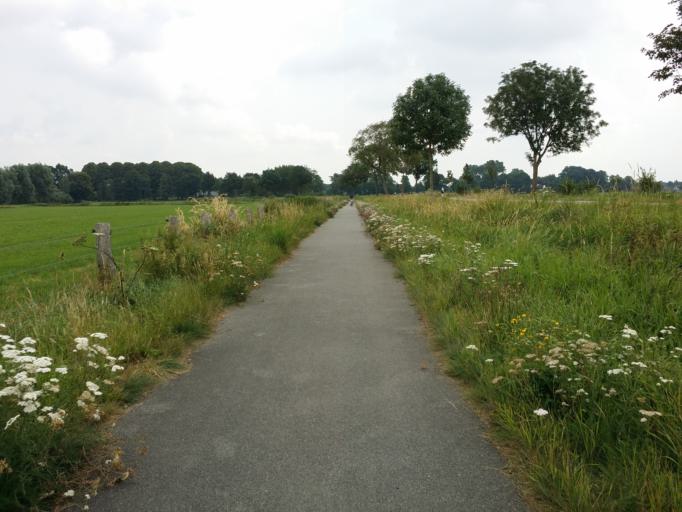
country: DE
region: Schleswig-Holstein
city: Krempermoor
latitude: 53.8763
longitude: 9.4669
